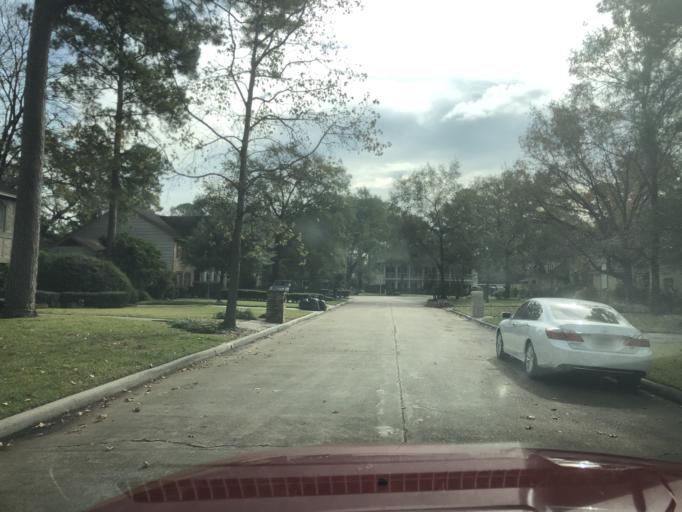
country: US
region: Texas
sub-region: Harris County
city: Spring
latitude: 30.0182
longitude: -95.4622
